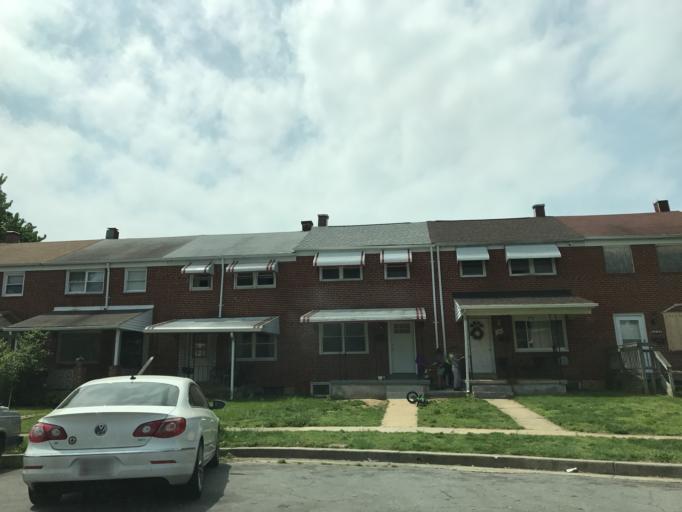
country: US
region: Maryland
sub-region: Baltimore County
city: Essex
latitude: 39.3080
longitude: -76.4485
